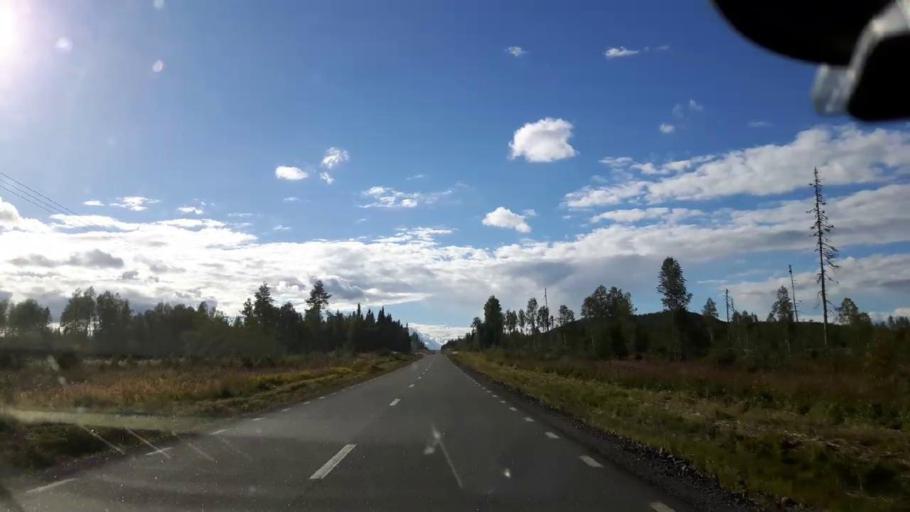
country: SE
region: Jaemtland
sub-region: Stroemsunds Kommun
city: Stroemsund
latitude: 63.5413
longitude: 15.9572
